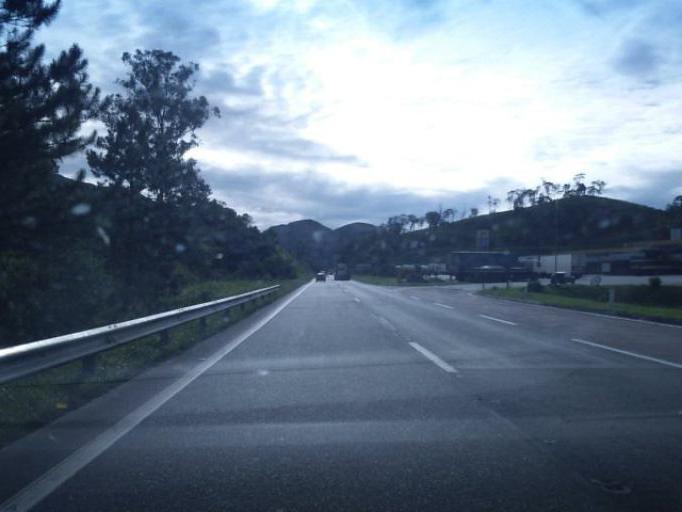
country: BR
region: Parana
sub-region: Campina Grande Do Sul
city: Campina Grande do Sul
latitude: -25.1079
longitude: -48.7924
